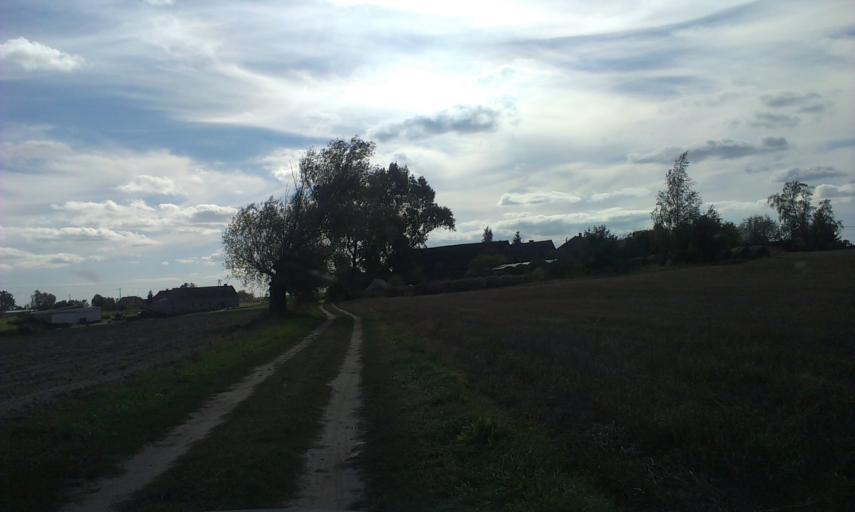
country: PL
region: Greater Poland Voivodeship
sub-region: Powiat zlotowski
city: Zakrzewo
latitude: 53.3007
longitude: 17.1472
